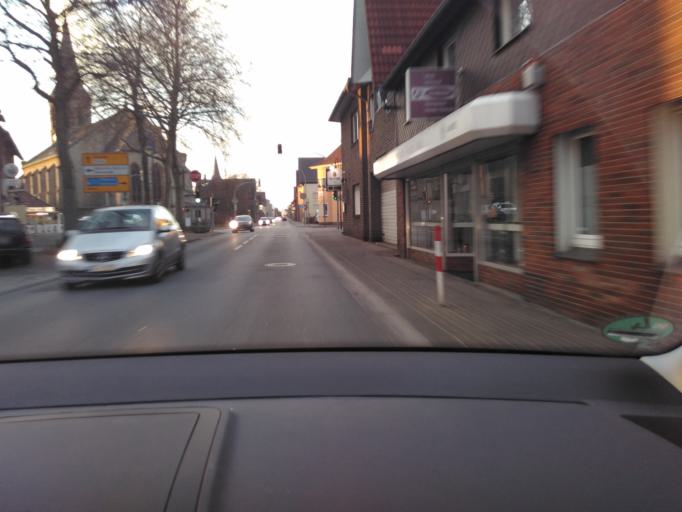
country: DE
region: North Rhine-Westphalia
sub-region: Regierungsbezirk Detmold
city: Verl
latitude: 51.9354
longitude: 8.4890
